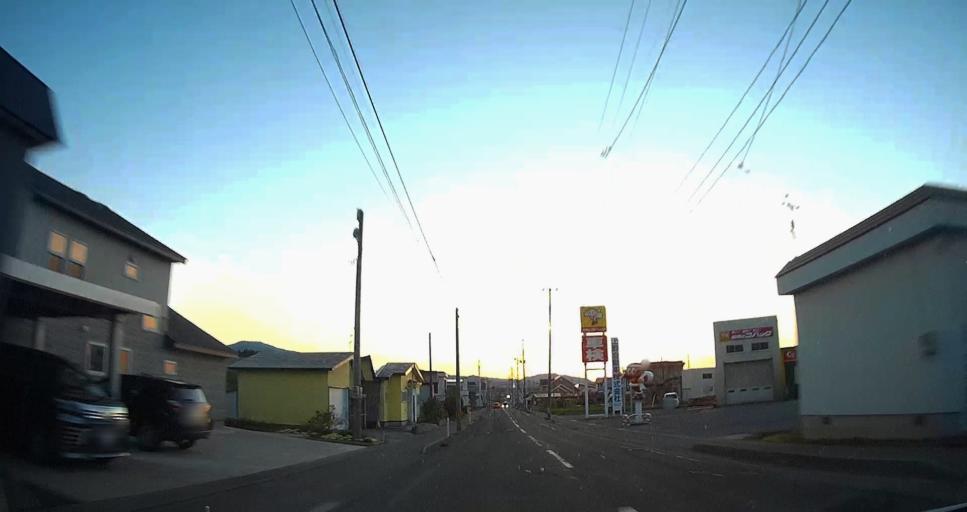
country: JP
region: Aomori
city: Misawa
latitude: 40.8688
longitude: 141.1190
